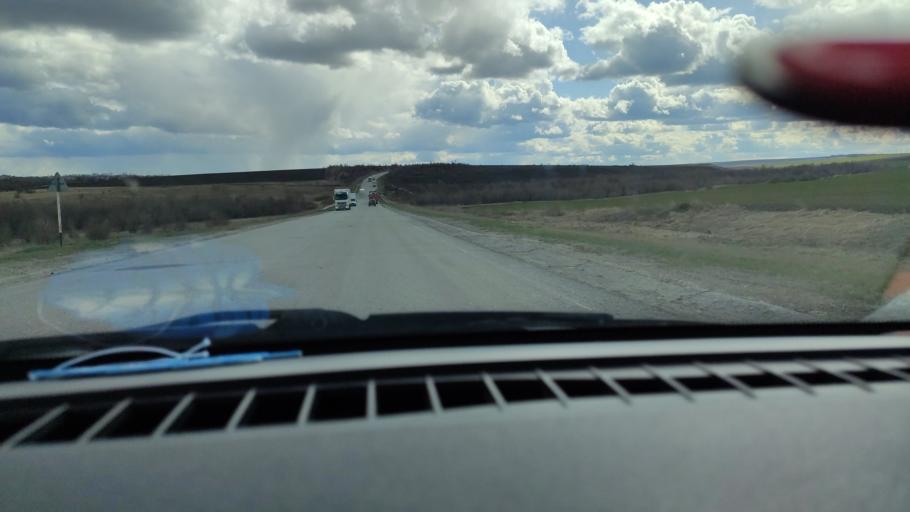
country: RU
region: Samara
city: Varlamovo
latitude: 53.0709
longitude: 48.3538
